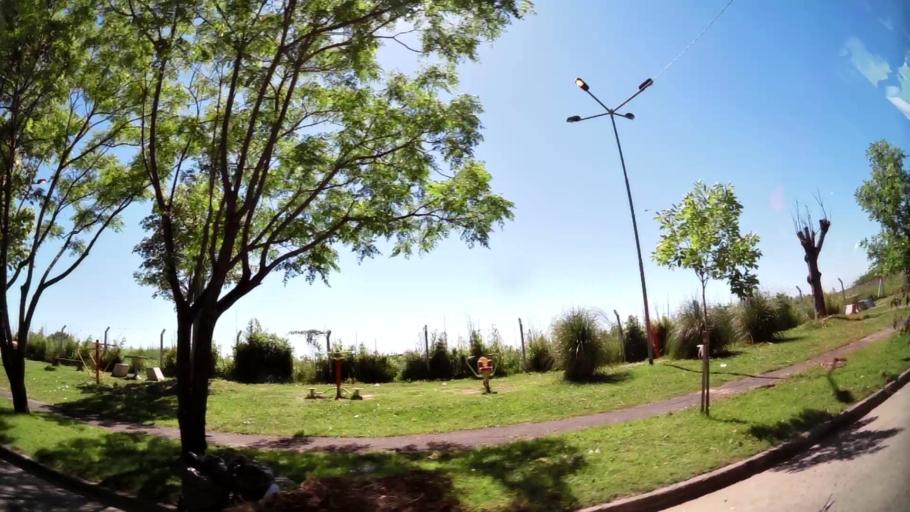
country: AR
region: Buenos Aires
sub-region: Partido de Tigre
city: Tigre
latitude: -34.5042
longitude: -58.6100
